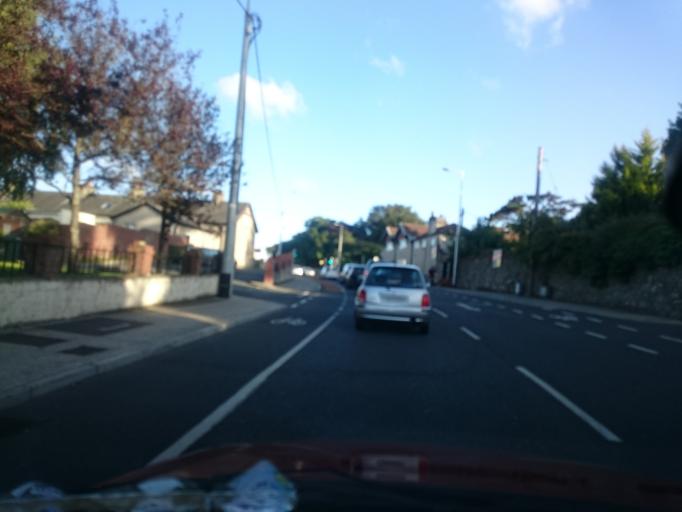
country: IE
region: Leinster
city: Balally
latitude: 53.2782
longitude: -6.2313
